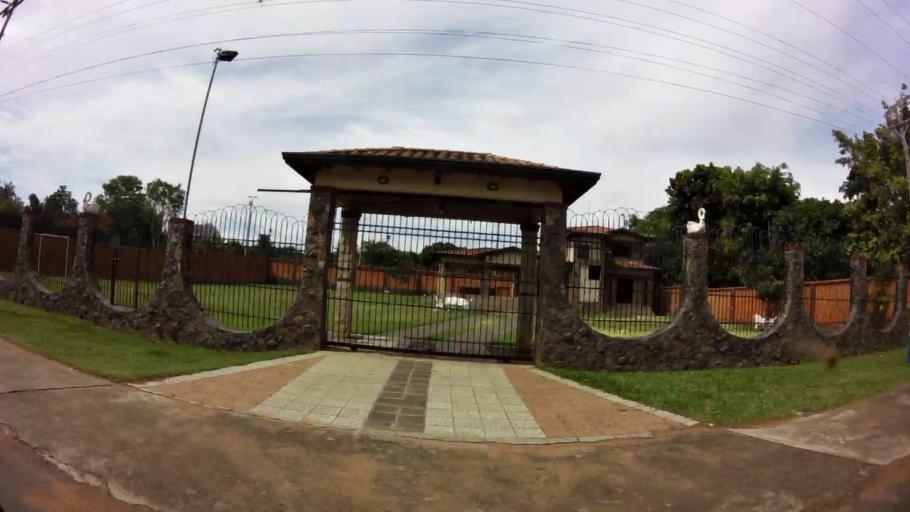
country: PY
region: Central
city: Limpio
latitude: -25.1813
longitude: -57.4469
